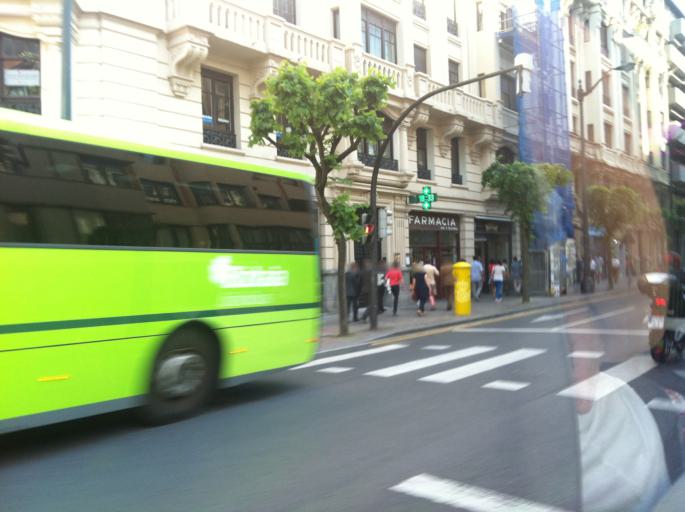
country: ES
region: Basque Country
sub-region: Bizkaia
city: Bilbao
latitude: 43.2651
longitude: -2.9340
